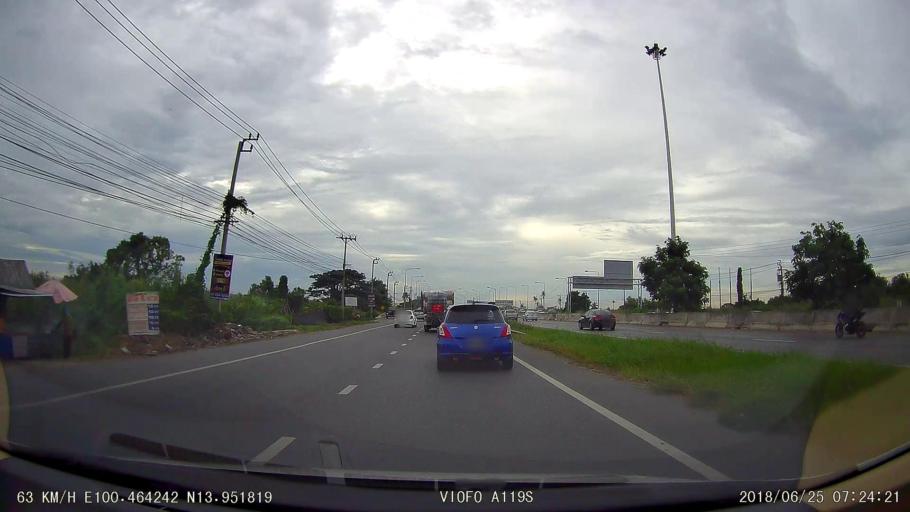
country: TH
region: Nonthaburi
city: Pak Kret
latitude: 13.9518
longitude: 100.4644
